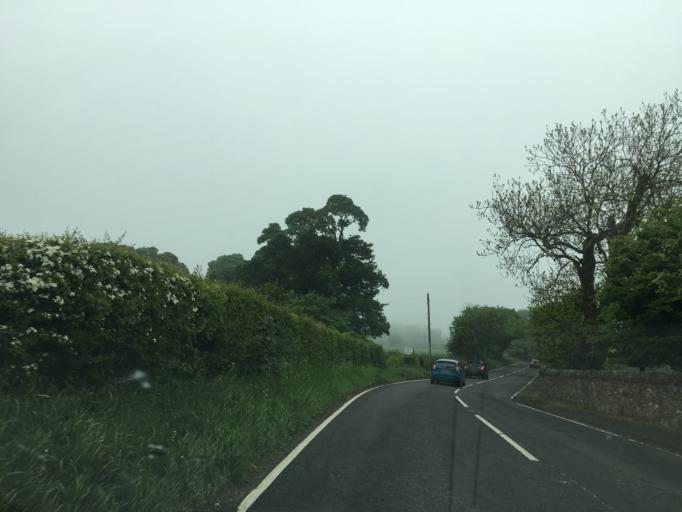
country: GB
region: Scotland
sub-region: Midlothian
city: Penicuik
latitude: 55.8374
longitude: -3.1997
